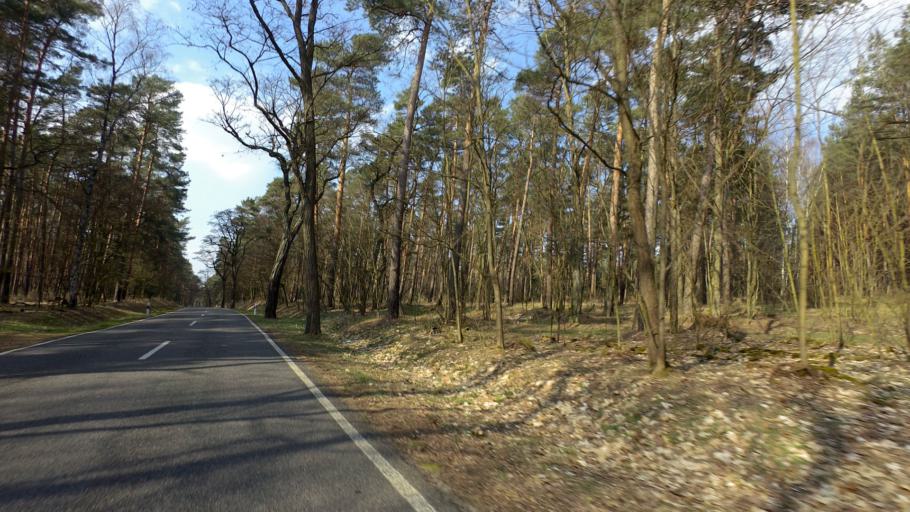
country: DE
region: Brandenburg
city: Dahme
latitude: 51.9311
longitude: 13.4541
